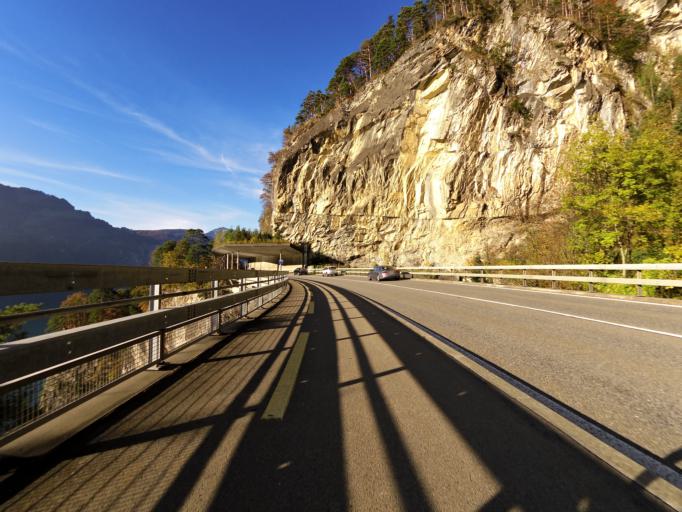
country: CH
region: Uri
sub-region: Uri
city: Flueelen
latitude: 46.9273
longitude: 8.6130
